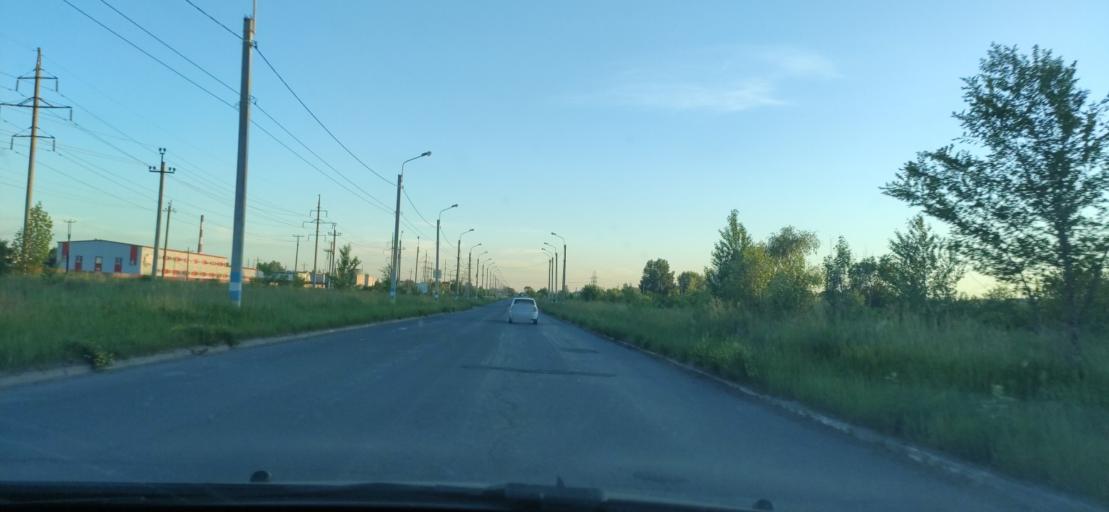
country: RU
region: Ulyanovsk
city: Mirnyy
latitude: 54.3730
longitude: 48.6497
